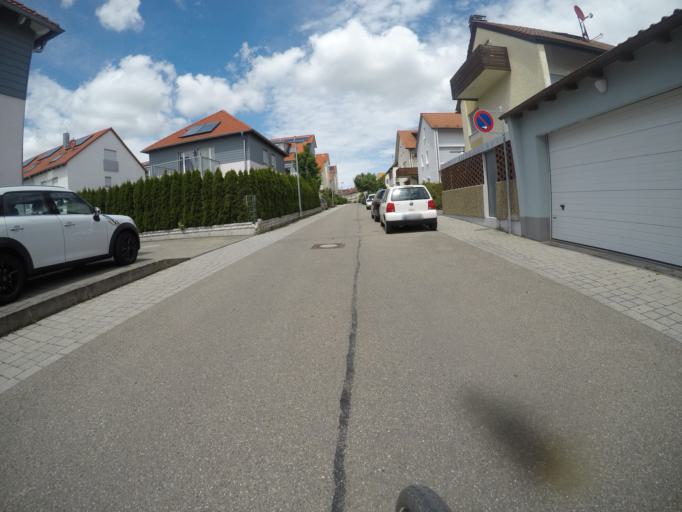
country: DE
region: Baden-Wuerttemberg
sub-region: Regierungsbezirk Stuttgart
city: Herrenberg
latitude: 48.5910
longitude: 8.8653
